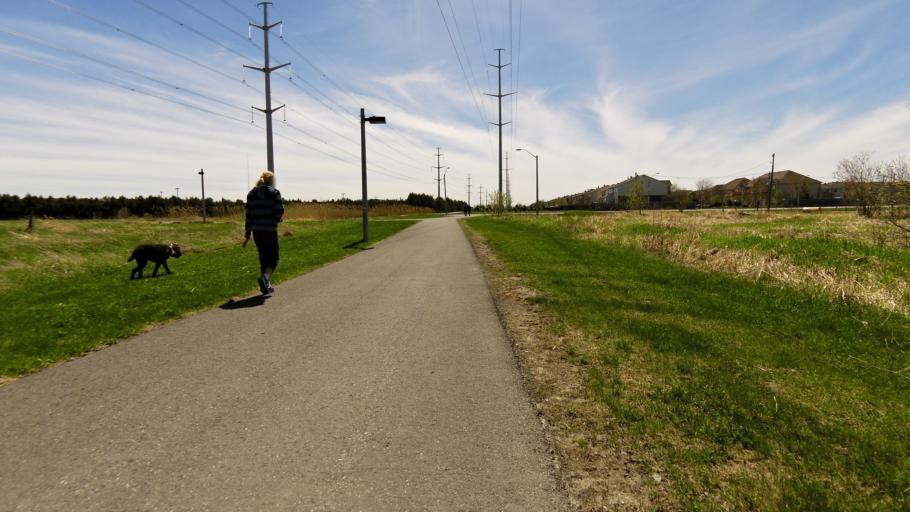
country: CA
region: Ontario
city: Clarence-Rockland
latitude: 45.4761
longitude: -75.4600
